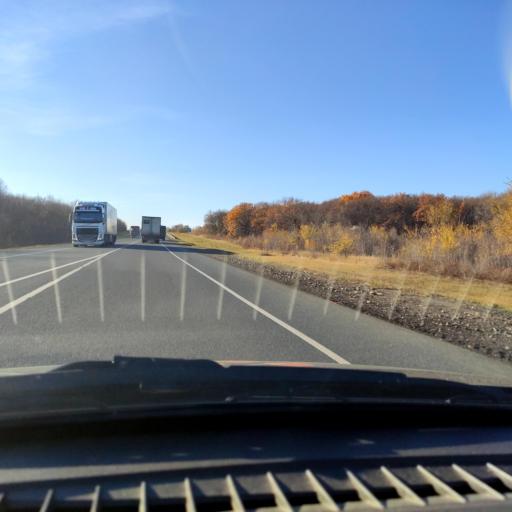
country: RU
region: Samara
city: Mezhdurechensk
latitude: 53.2587
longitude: 49.0950
